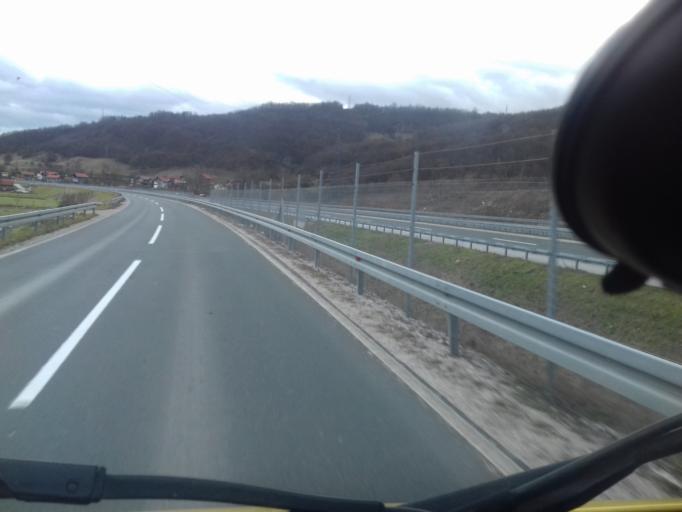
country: BA
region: Federation of Bosnia and Herzegovina
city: Kakanj
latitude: 44.1316
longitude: 18.0614
